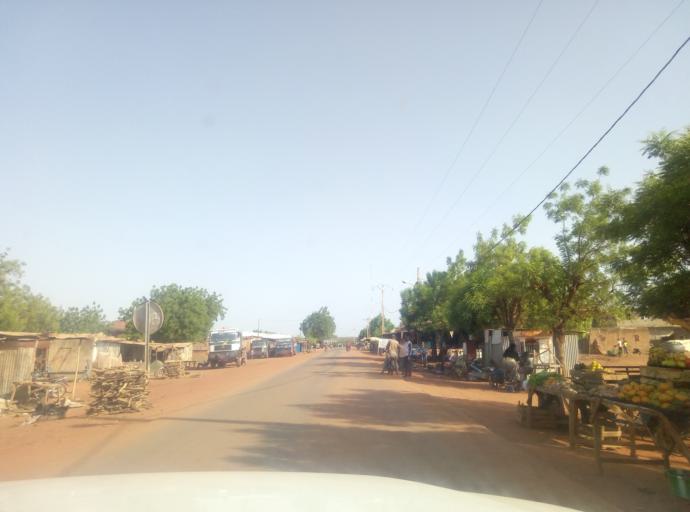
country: ML
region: Bamako
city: Bamako
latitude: 12.6147
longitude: -7.7775
